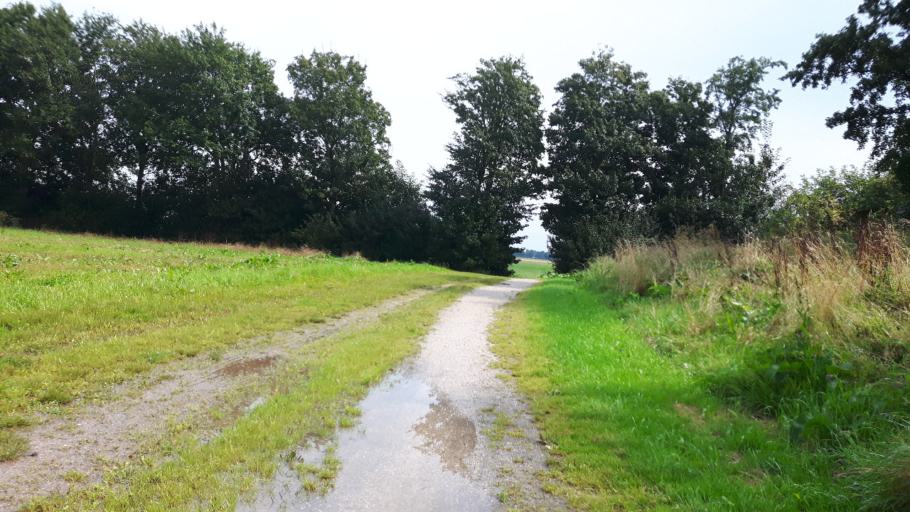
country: NL
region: Flevoland
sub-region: Gemeente Noordoostpolder
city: Ens
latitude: 52.6205
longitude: 5.7733
